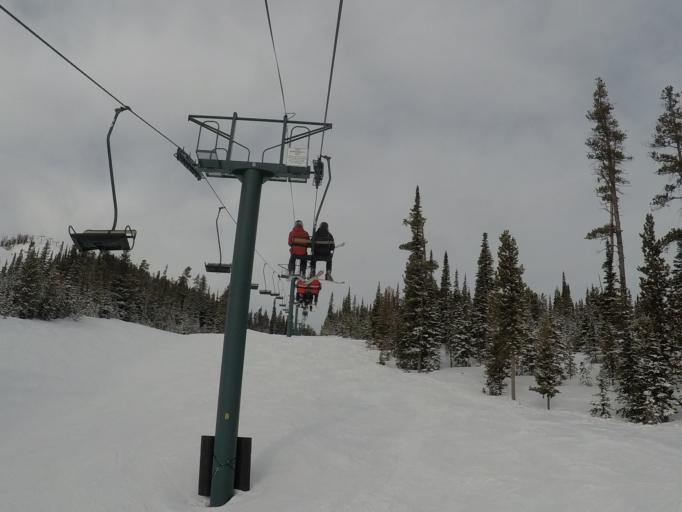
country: US
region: Montana
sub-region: Meagher County
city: White Sulphur Springs
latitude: 46.8396
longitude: -110.7085
